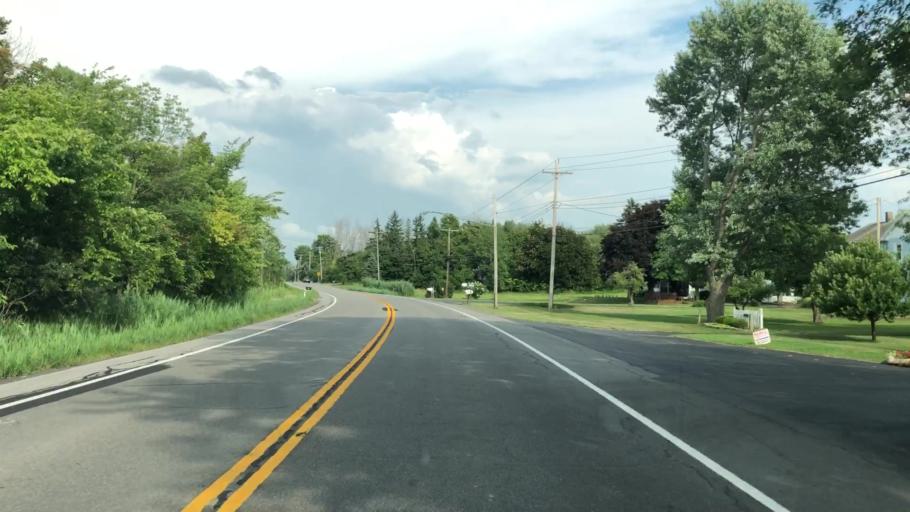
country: US
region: New York
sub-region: Erie County
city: Elma Center
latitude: 42.8554
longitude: -78.6678
